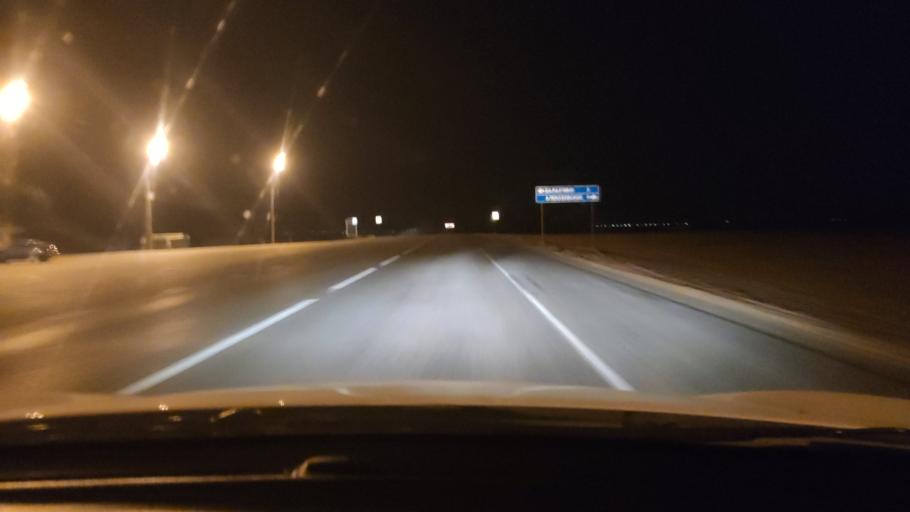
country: RU
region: Tatarstan
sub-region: Alekseyevskiy Rayon
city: Alekseyevskoye
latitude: 55.2908
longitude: 49.9706
